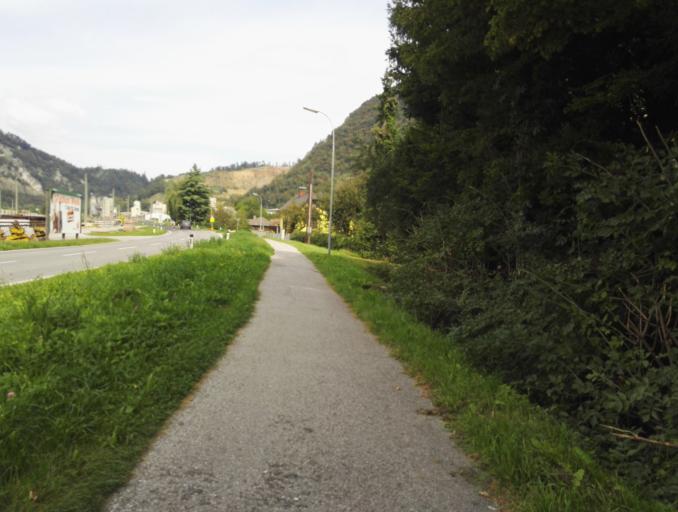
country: AT
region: Styria
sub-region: Politischer Bezirk Graz-Umgebung
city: Peggau
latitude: 47.2097
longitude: 15.3434
